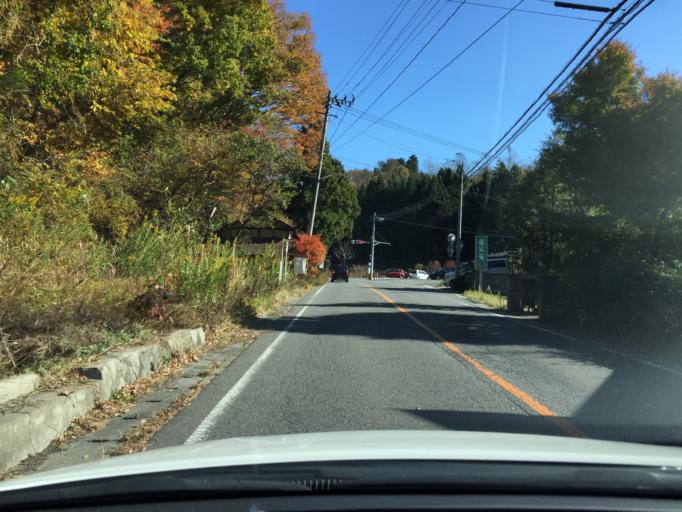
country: JP
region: Fukushima
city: Funehikimachi-funehiki
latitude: 37.4110
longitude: 140.5409
